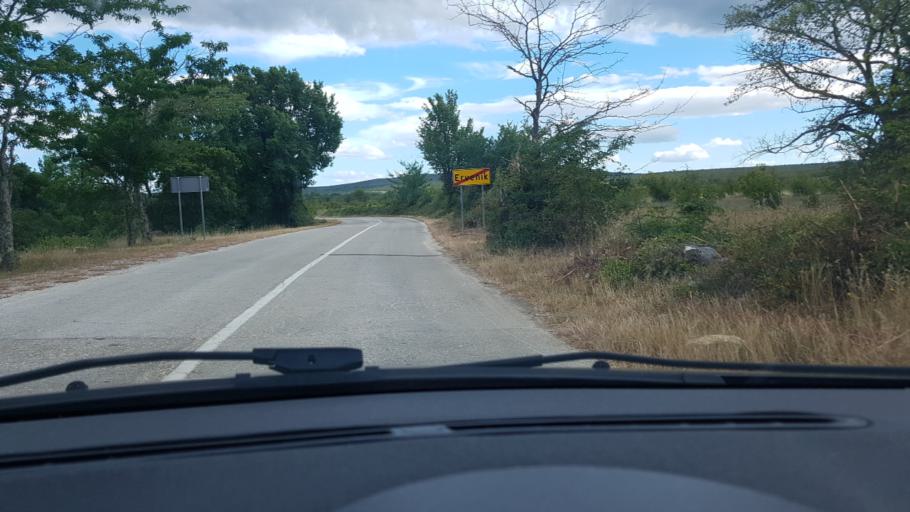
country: HR
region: Sibensko-Kniniska
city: Kistanje
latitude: 44.1062
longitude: 15.9410
